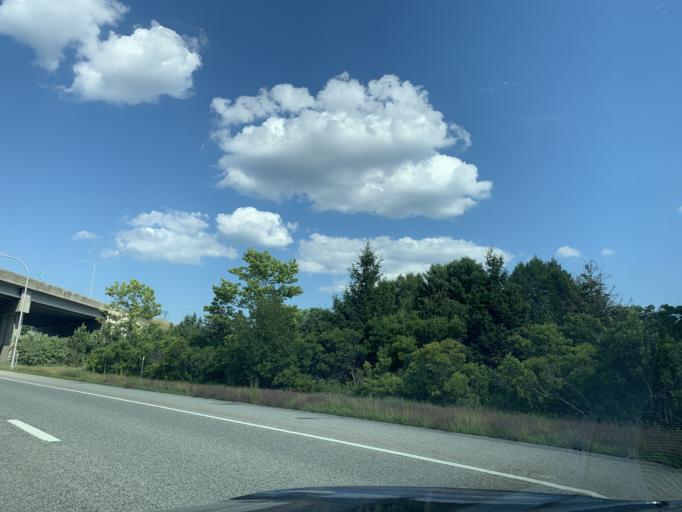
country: US
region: Rhode Island
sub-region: Washington County
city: North Kingstown
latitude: 41.6033
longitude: -71.4511
